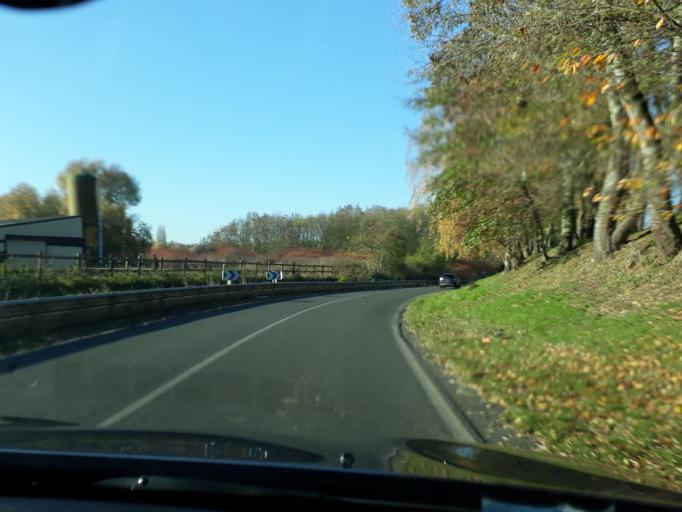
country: FR
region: Nord-Pas-de-Calais
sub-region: Departement du Nord
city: Sin-le-Noble
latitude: 50.3614
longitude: 3.1312
